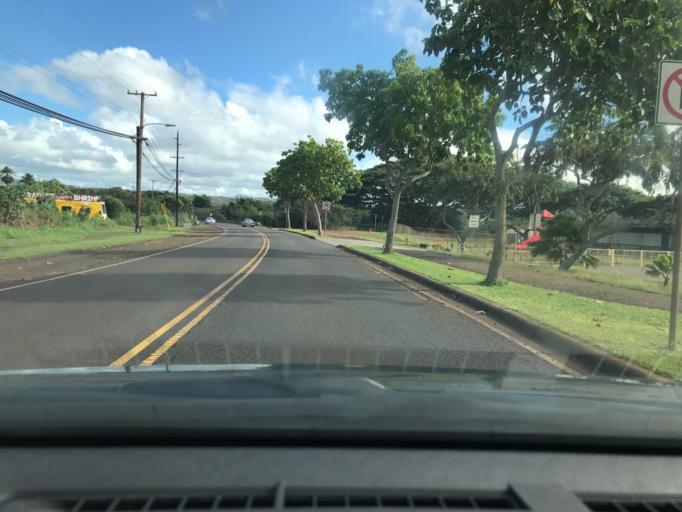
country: US
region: Hawaii
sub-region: Honolulu County
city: Waialua
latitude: 21.5763
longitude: -158.1214
